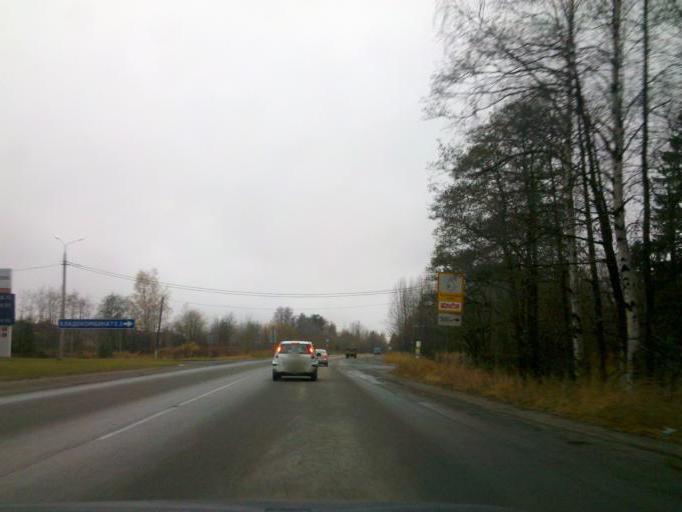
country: RU
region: Republic of Karelia
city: Petrozavodsk
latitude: 61.8210
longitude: 34.2436
